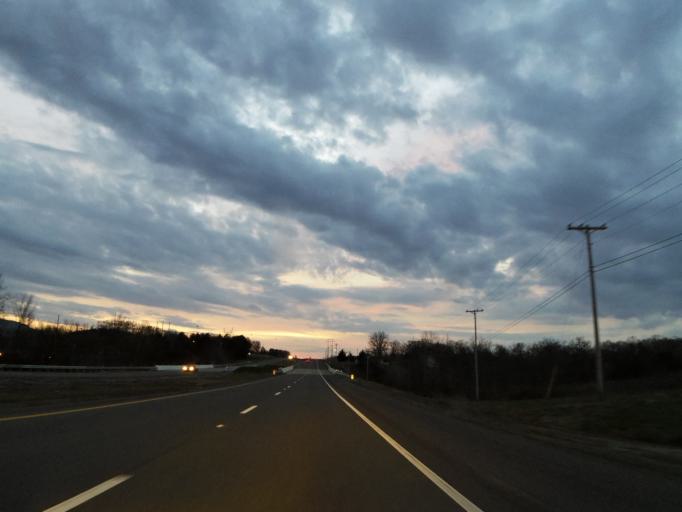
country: US
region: Tennessee
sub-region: Polk County
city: Benton
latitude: 35.2211
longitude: -84.5880
